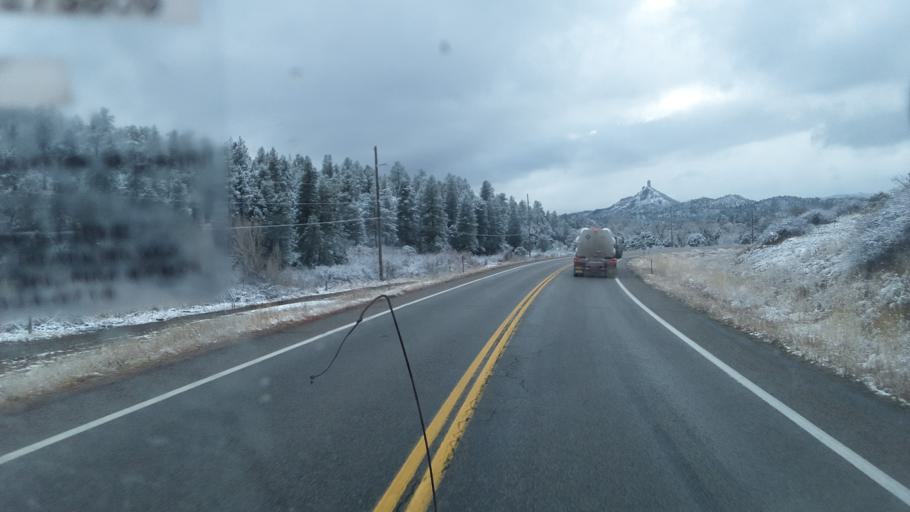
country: US
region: Colorado
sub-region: Archuleta County
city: Pagosa Springs
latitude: 37.2072
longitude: -107.2424
